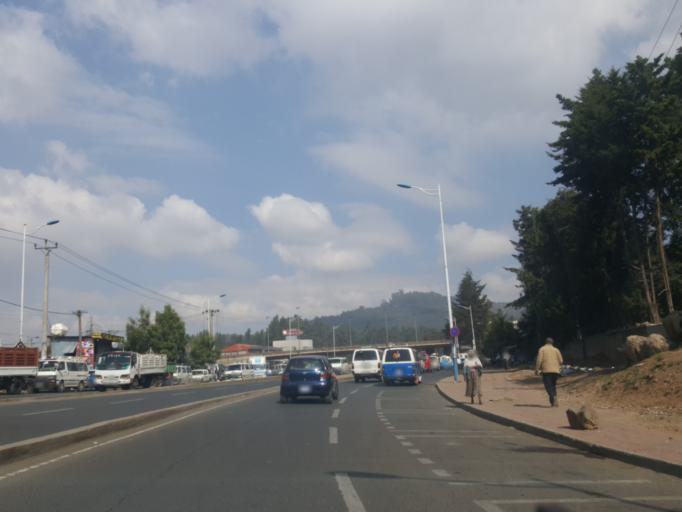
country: ET
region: Adis Abeba
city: Addis Ababa
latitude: 9.0550
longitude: 38.7140
